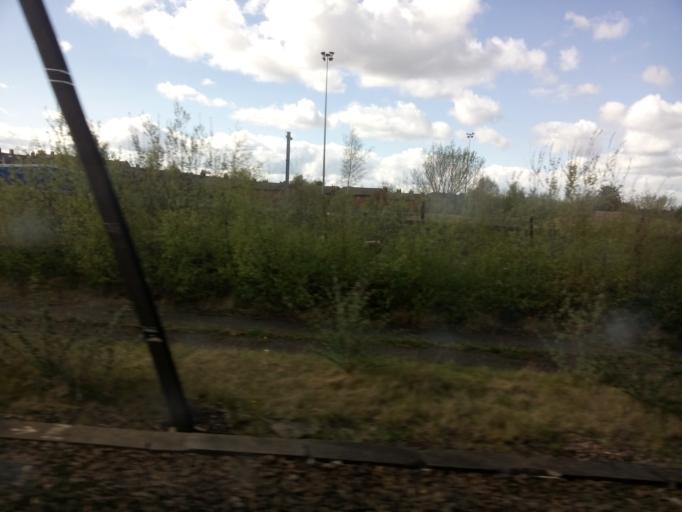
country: GB
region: England
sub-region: Gateshead
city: Felling
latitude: 54.9836
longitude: -1.5718
